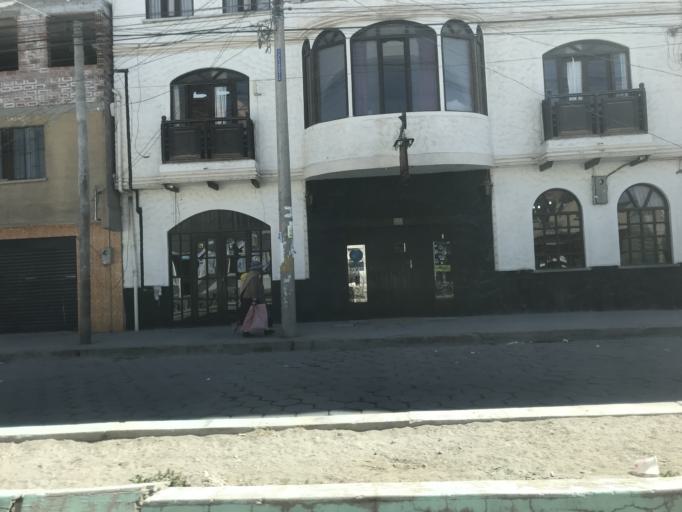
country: BO
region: Potosi
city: Uyuni
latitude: -20.4607
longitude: -66.8237
